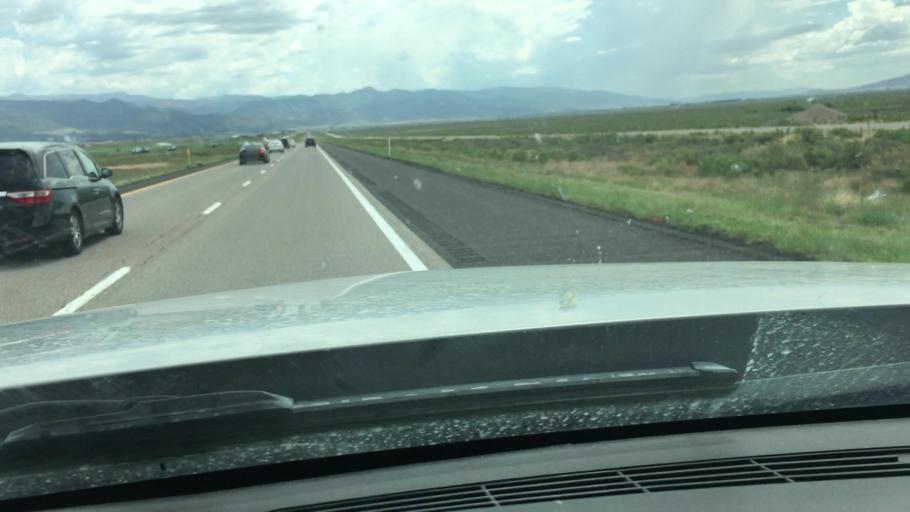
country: US
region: Utah
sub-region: Iron County
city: Parowan
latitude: 37.9533
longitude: -112.7531
